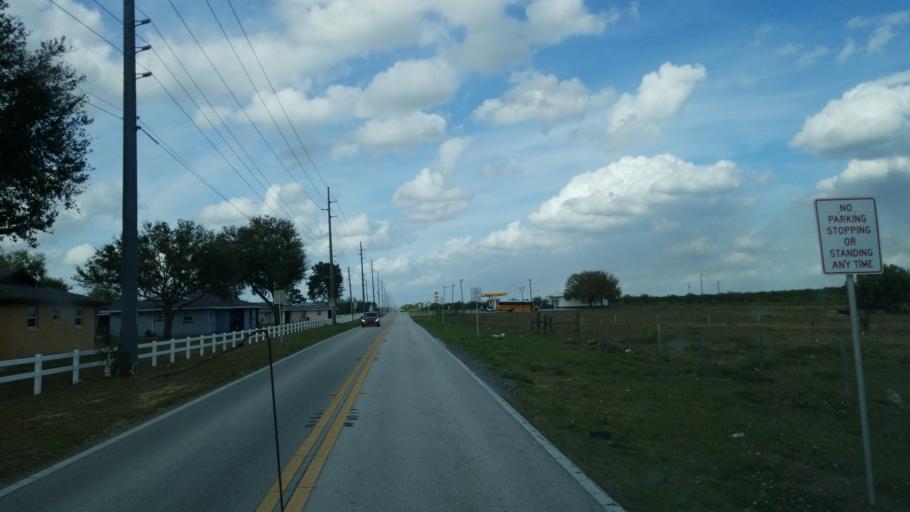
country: US
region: Florida
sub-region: Polk County
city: Haines City
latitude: 28.1191
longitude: -81.5904
